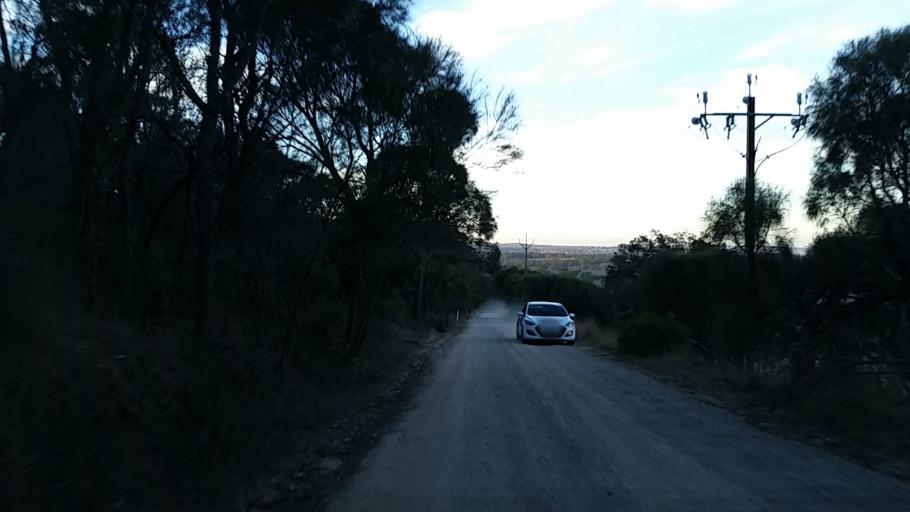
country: AU
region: South Australia
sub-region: Mount Barker
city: Nairne
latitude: -35.0630
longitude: 138.9239
